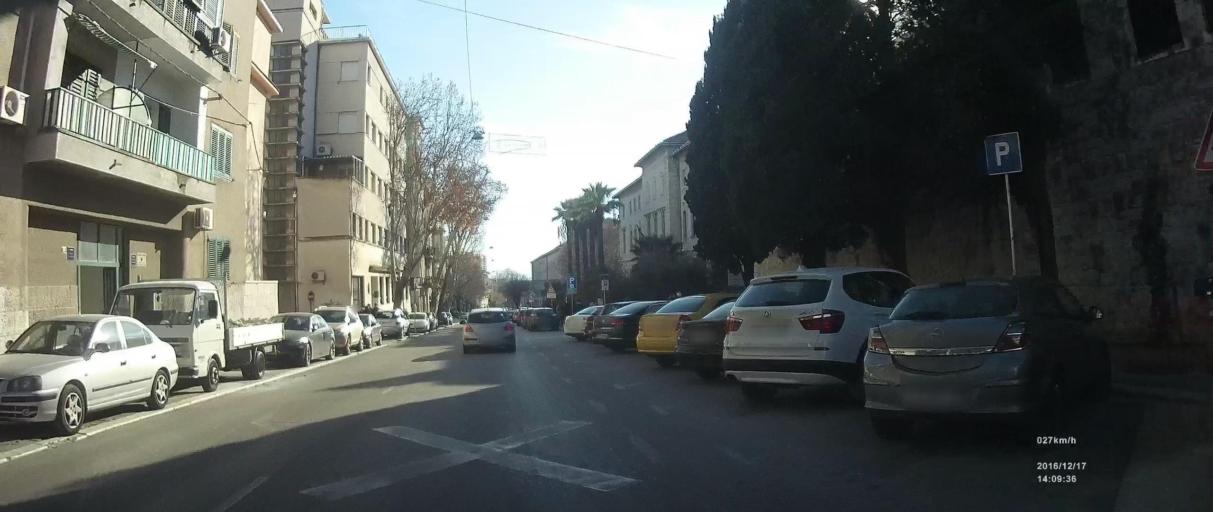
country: HR
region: Splitsko-Dalmatinska
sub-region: Grad Split
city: Split
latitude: 43.5158
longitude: 16.4354
